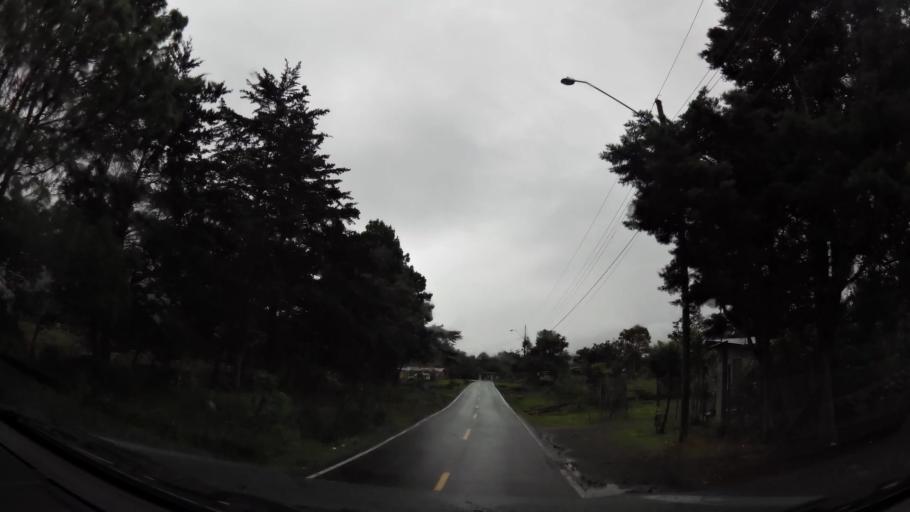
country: PA
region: Chiriqui
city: Volcan
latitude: 8.7925
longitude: -82.6496
